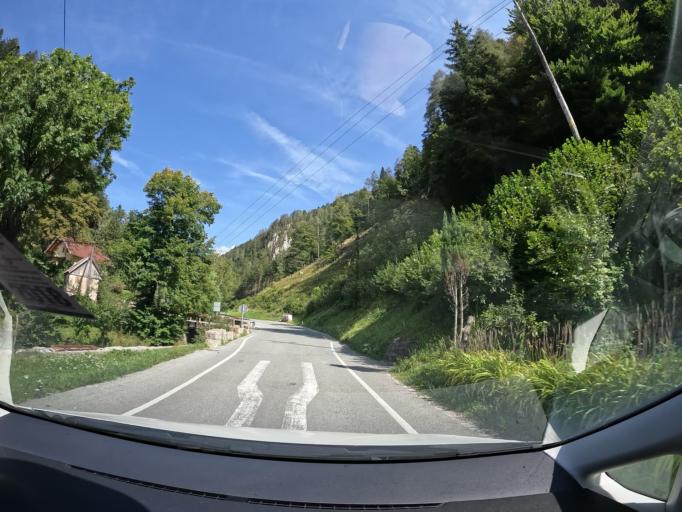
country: SI
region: Jesenice
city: Koroska Bela
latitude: 46.4667
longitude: 14.0972
